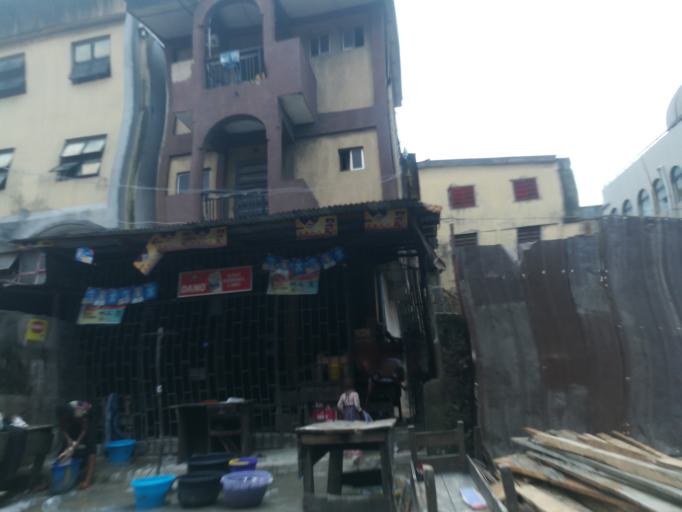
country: NG
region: Lagos
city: Lagos
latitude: 6.4611
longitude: 3.3847
